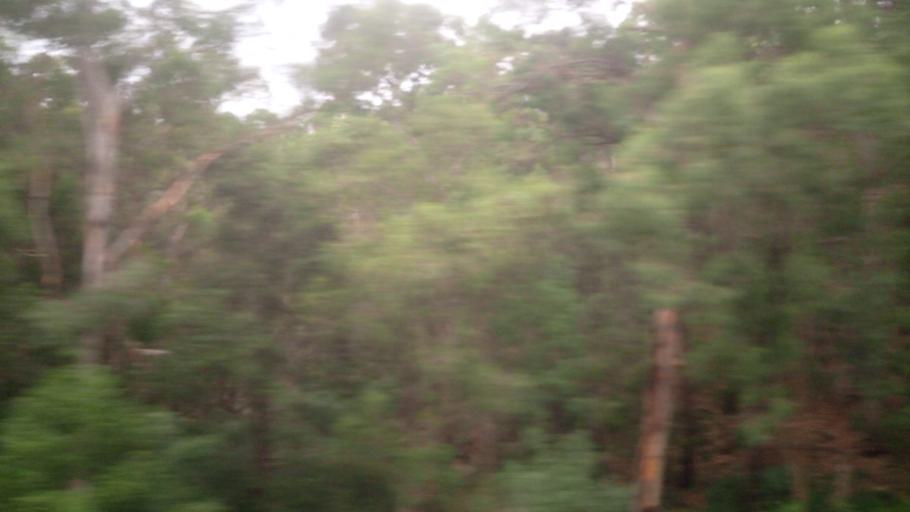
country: AU
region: New South Wales
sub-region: Blue Mountains Municipality
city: Glenbrook
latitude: -33.7655
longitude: 150.6424
